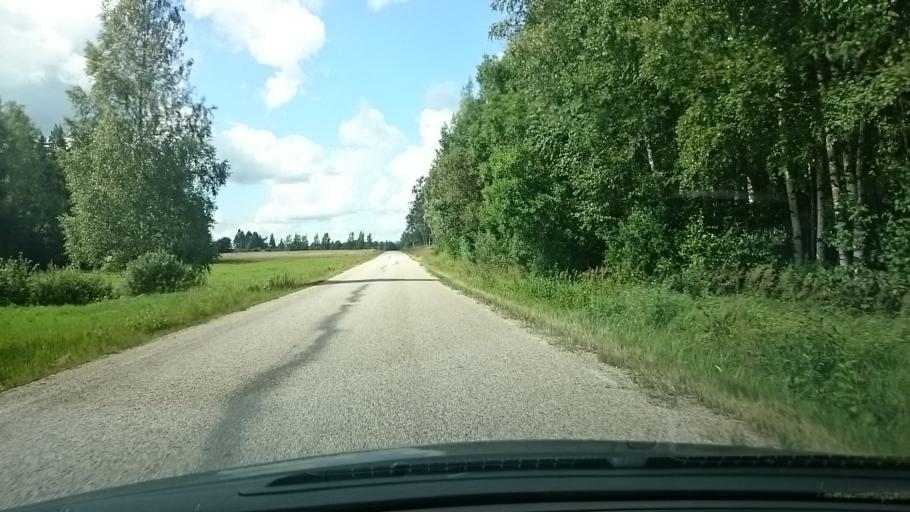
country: EE
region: Vorumaa
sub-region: Voru linn
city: Voru
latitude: 57.9195
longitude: 27.1492
